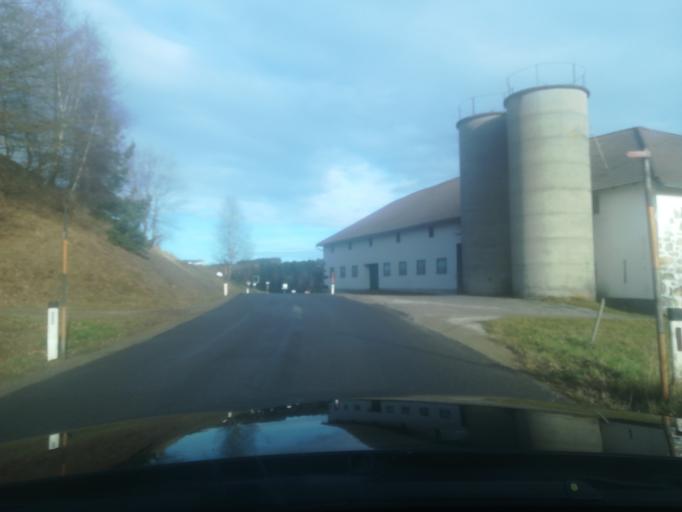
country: AT
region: Upper Austria
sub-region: Politischer Bezirk Perg
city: Perg
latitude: 48.3474
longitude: 14.6213
